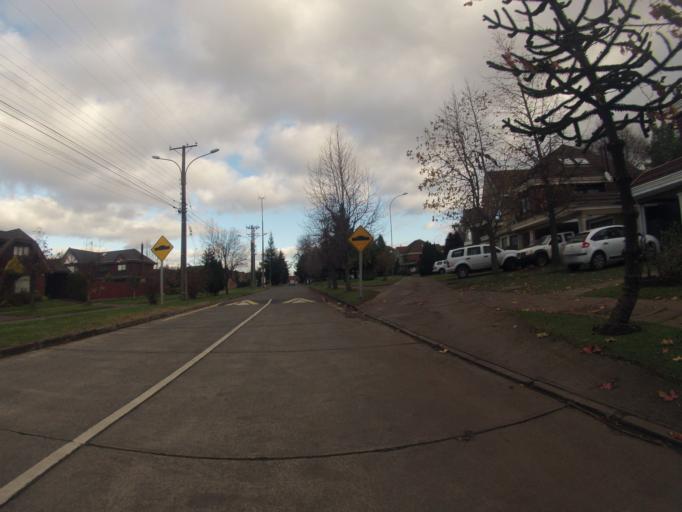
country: CL
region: Araucania
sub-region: Provincia de Cautin
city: Temuco
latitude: -38.7382
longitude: -72.6409
